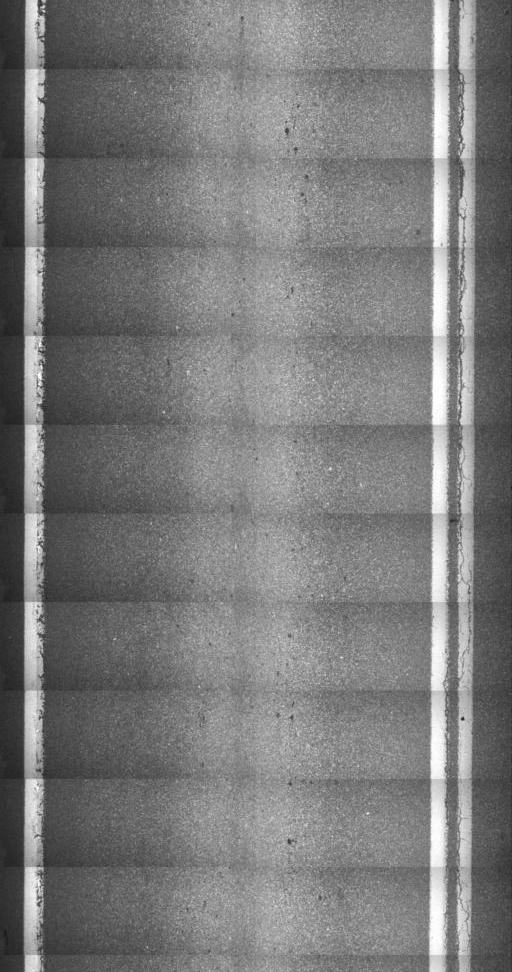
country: US
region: New York
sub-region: Washington County
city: Granville
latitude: 43.3429
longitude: -73.1770
